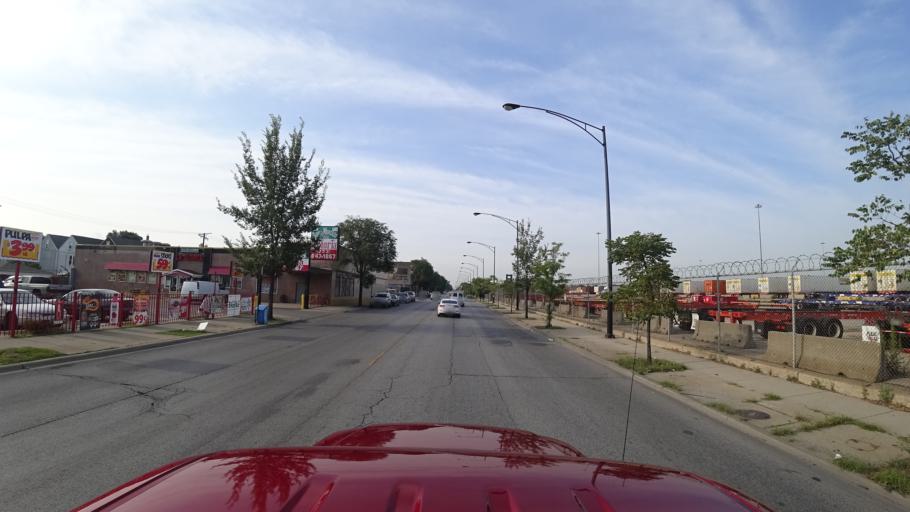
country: US
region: Illinois
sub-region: Cook County
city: Cicero
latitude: 41.8188
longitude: -87.7044
